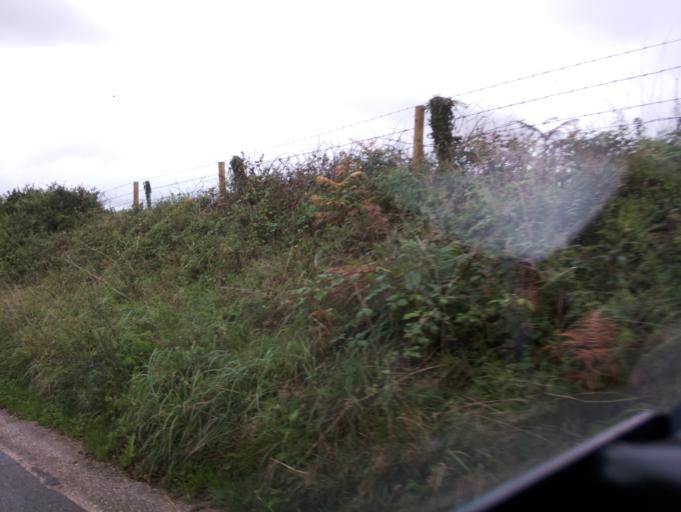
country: GB
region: England
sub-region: Devon
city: Dartmouth
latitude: 50.3454
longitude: -3.6382
